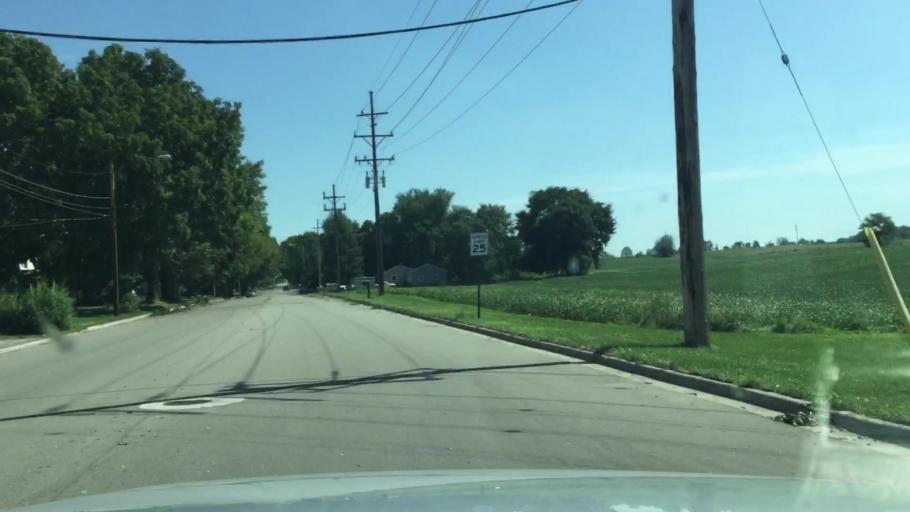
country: US
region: Michigan
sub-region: Lenawee County
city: Clinton
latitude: 42.0647
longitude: -83.9668
